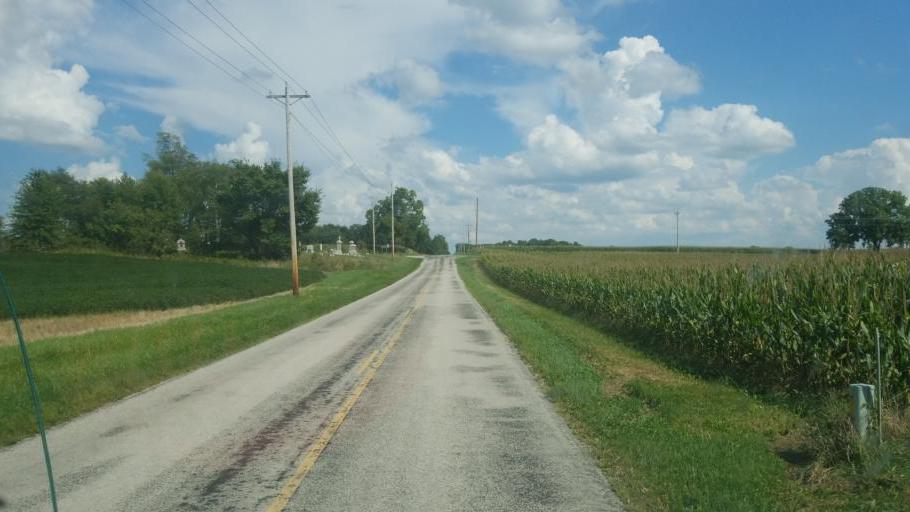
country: US
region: Ohio
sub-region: Seneca County
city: Tiffin
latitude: 40.9934
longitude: -83.1145
